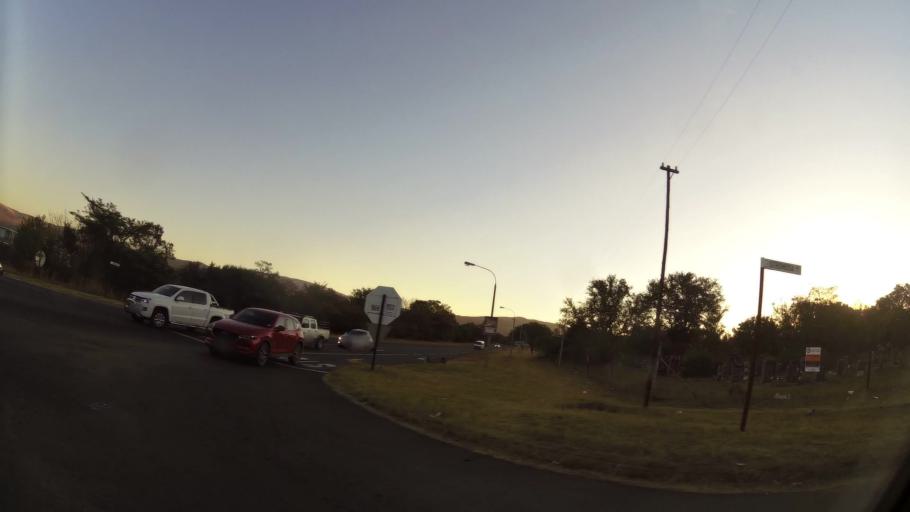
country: ZA
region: North-West
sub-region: Bojanala Platinum District Municipality
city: Rustenburg
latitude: -25.6710
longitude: 27.2174
